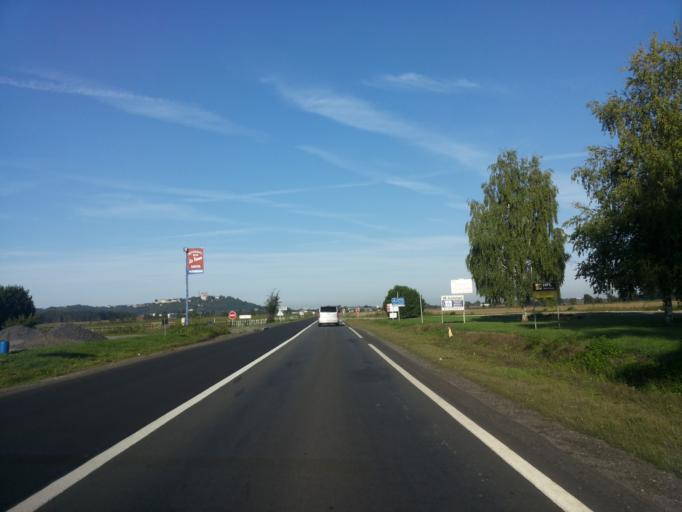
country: FR
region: Picardie
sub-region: Departement de l'Aisne
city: Athies-sous-Laon
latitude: 49.5638
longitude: 3.6811
